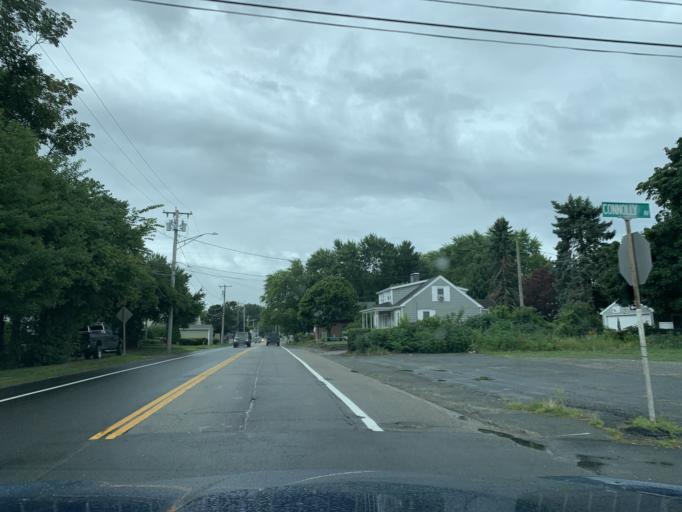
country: US
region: Rhode Island
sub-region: Bristol County
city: Warren
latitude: 41.7362
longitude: -71.2744
